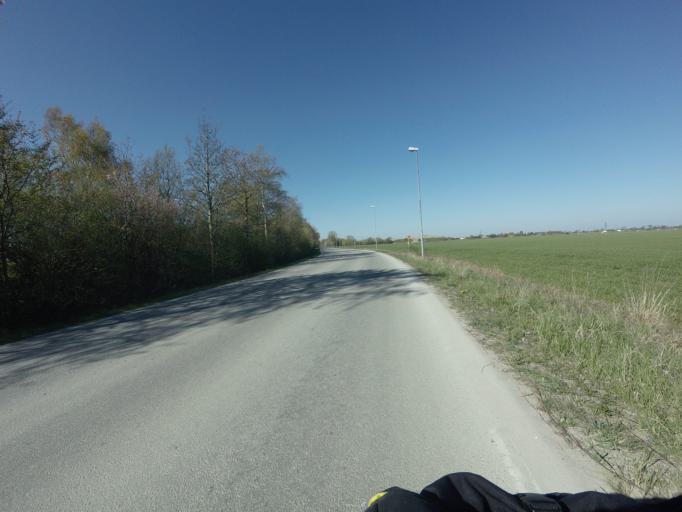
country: SE
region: Skane
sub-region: Staffanstorps Kommun
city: Hjaerup
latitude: 55.6659
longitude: 13.1096
